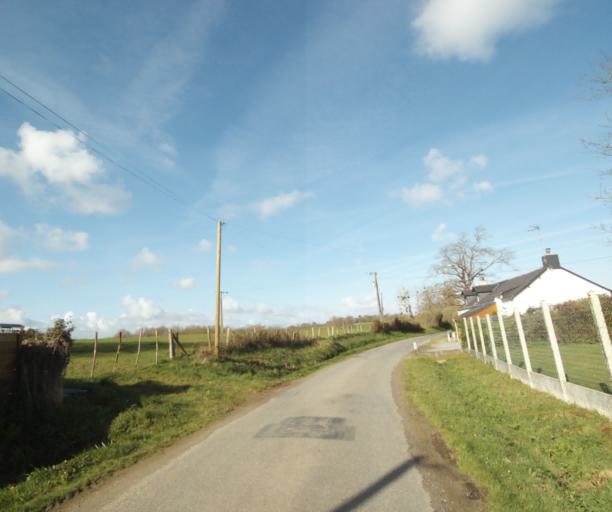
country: FR
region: Pays de la Loire
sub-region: Departement de la Loire-Atlantique
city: Bouvron
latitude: 47.4093
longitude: -1.8439
